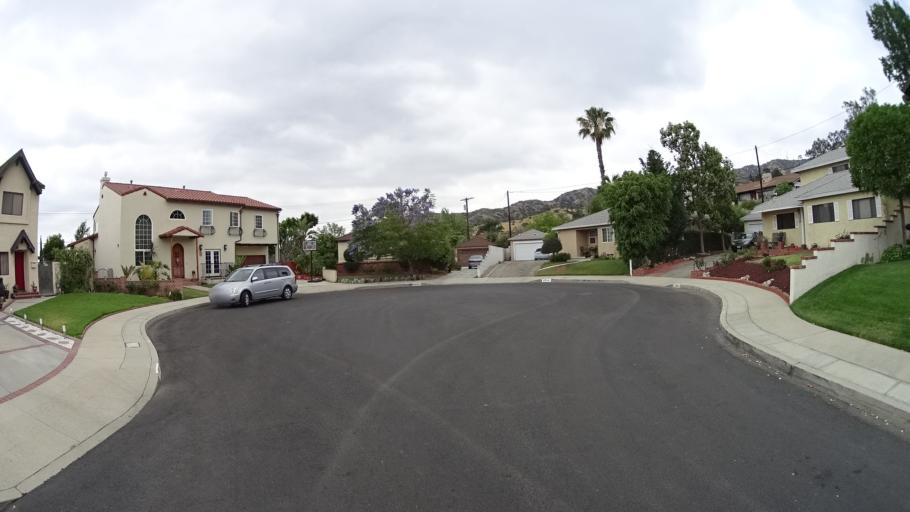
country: US
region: California
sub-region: Los Angeles County
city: Burbank
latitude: 34.2089
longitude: -118.3315
